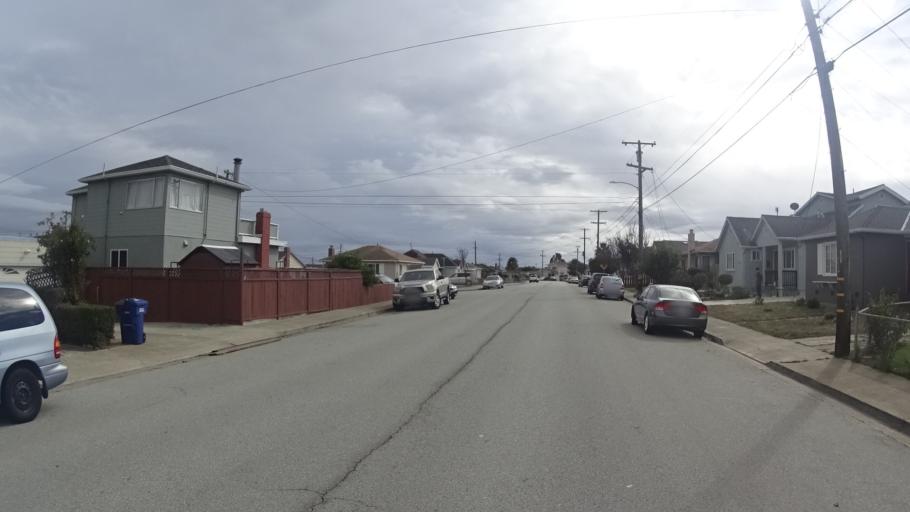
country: US
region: California
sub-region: San Mateo County
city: South San Francisco
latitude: 37.6500
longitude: -122.4245
